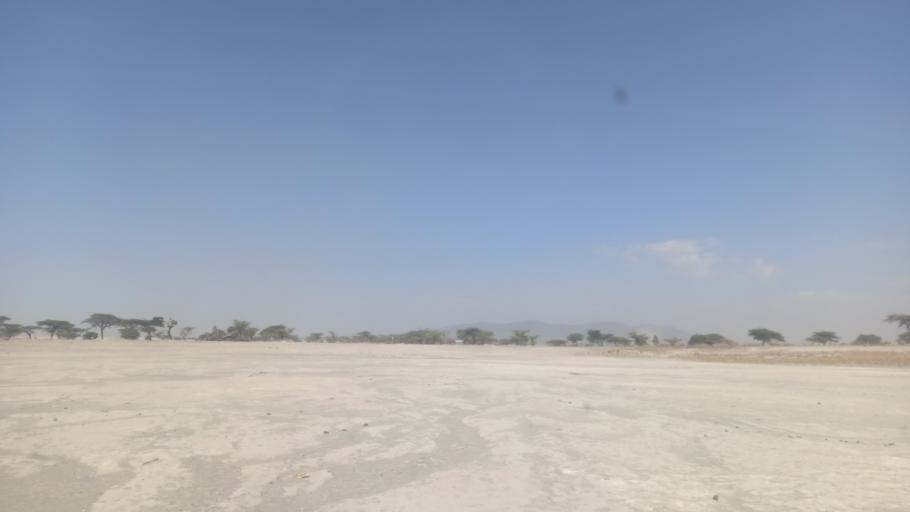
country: ET
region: Oromiya
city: Ziway
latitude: 7.6877
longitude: 38.6547
